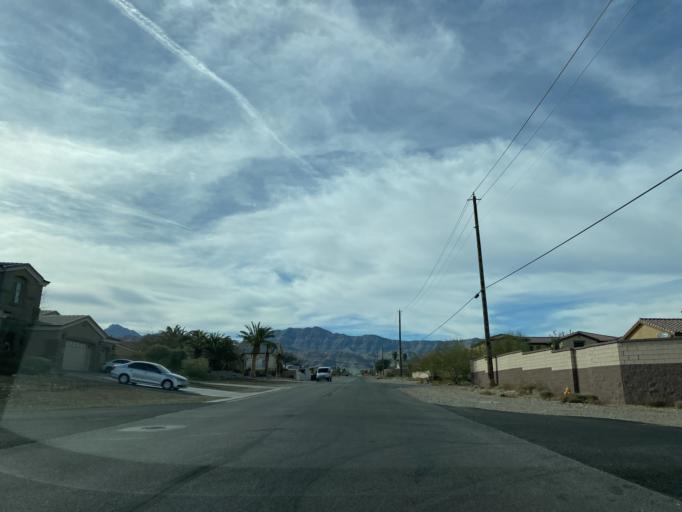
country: US
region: Nevada
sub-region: Clark County
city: Summerlin South
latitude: 36.2700
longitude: -115.3126
